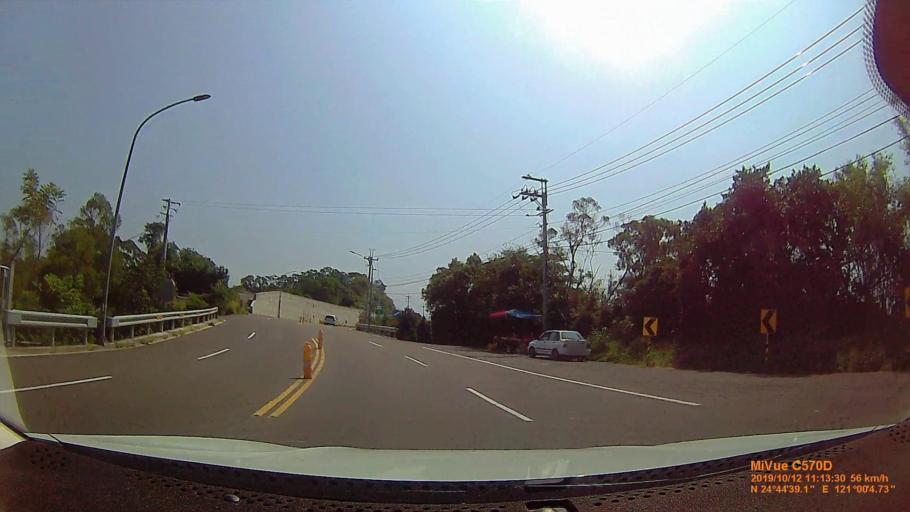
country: TW
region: Taiwan
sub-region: Hsinchu
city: Hsinchu
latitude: 24.7441
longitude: 121.0014
